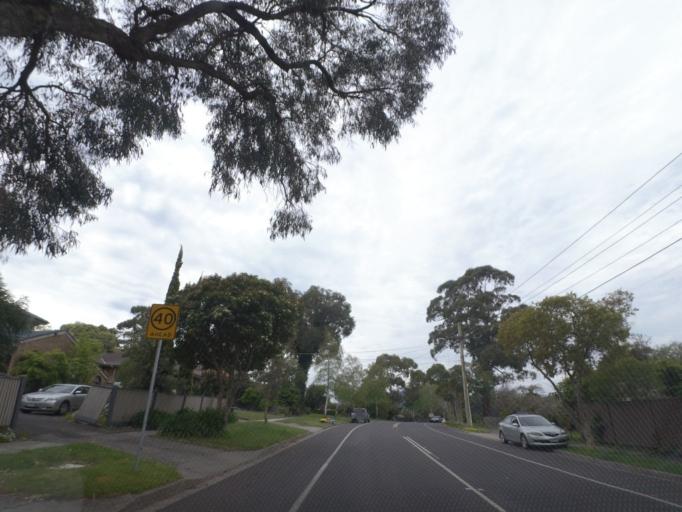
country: AU
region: Victoria
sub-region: Knox
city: The Basin
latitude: -37.8512
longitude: 145.3031
